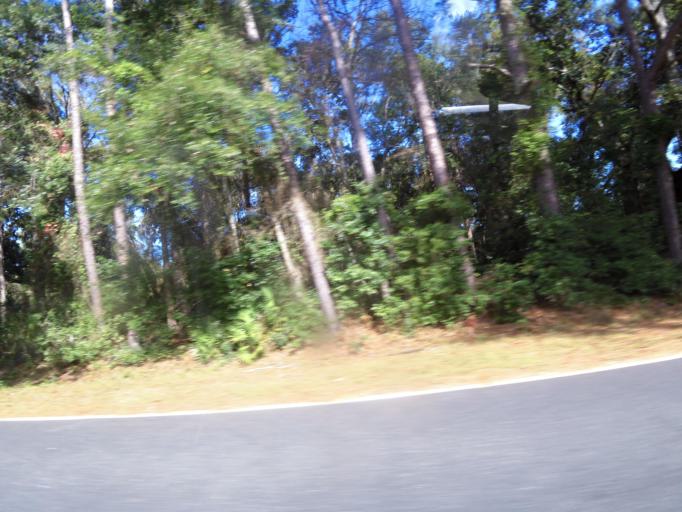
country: US
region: Georgia
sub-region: Glynn County
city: Brunswick
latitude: 31.1405
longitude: -81.5670
